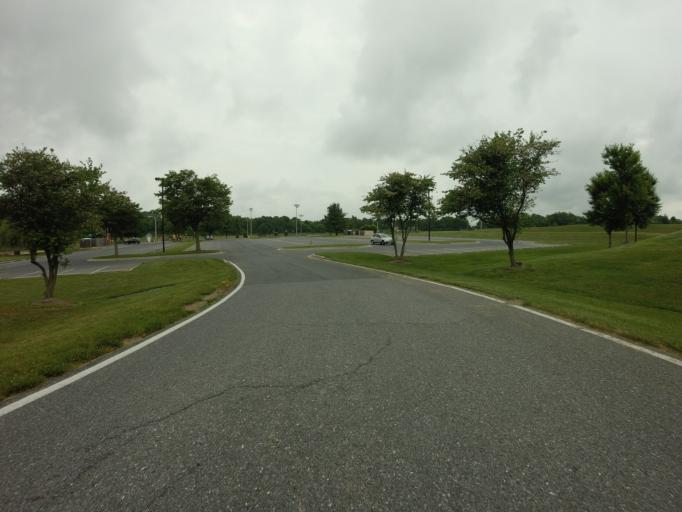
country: US
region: Maryland
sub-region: Frederick County
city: Ballenger Creek
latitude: 39.3825
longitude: -77.4468
